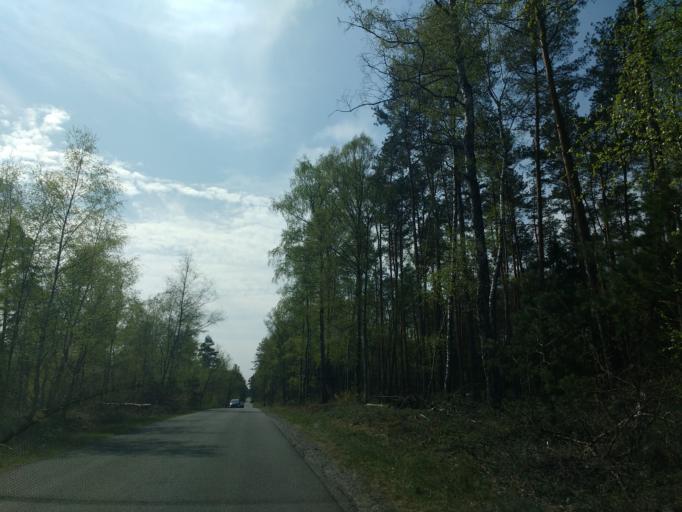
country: DE
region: North Rhine-Westphalia
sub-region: Regierungsbezirk Detmold
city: Hovelhof
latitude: 51.8487
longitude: 8.6841
